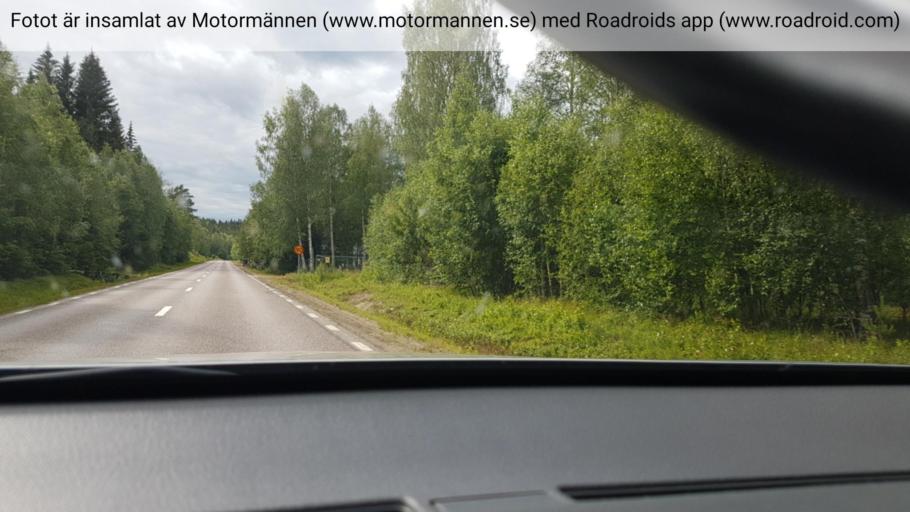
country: NO
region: Hedmark
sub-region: Trysil
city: Innbygda
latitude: 60.8990
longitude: 12.5876
